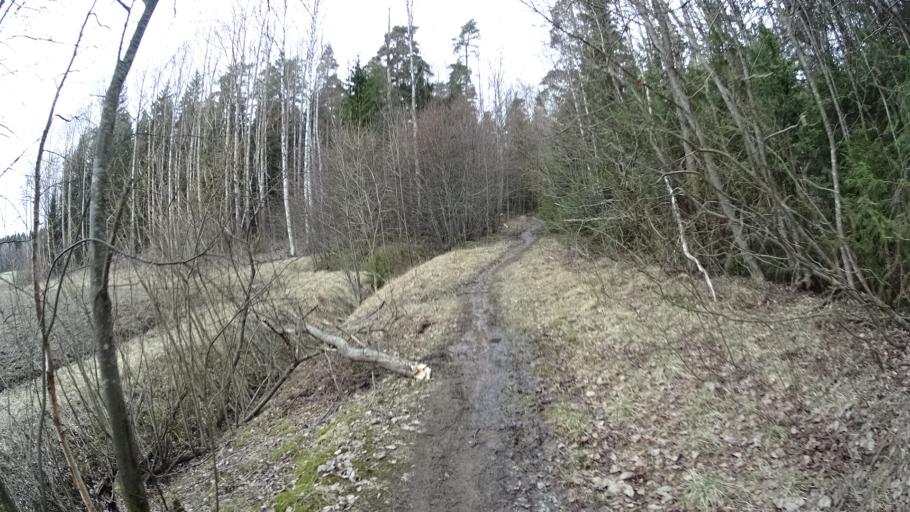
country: FI
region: Uusimaa
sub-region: Helsinki
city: Kilo
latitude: 60.2829
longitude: 24.8038
